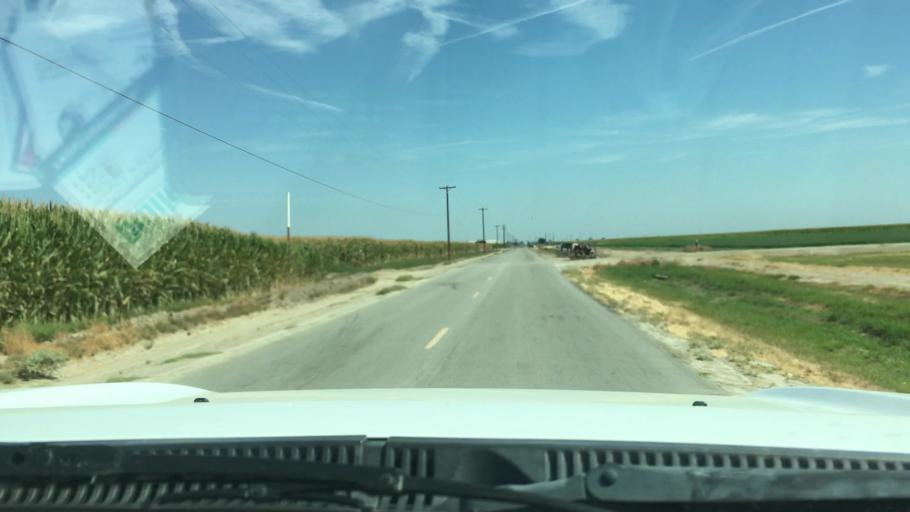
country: US
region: California
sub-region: Kern County
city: Buttonwillow
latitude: 35.4018
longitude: -119.3767
